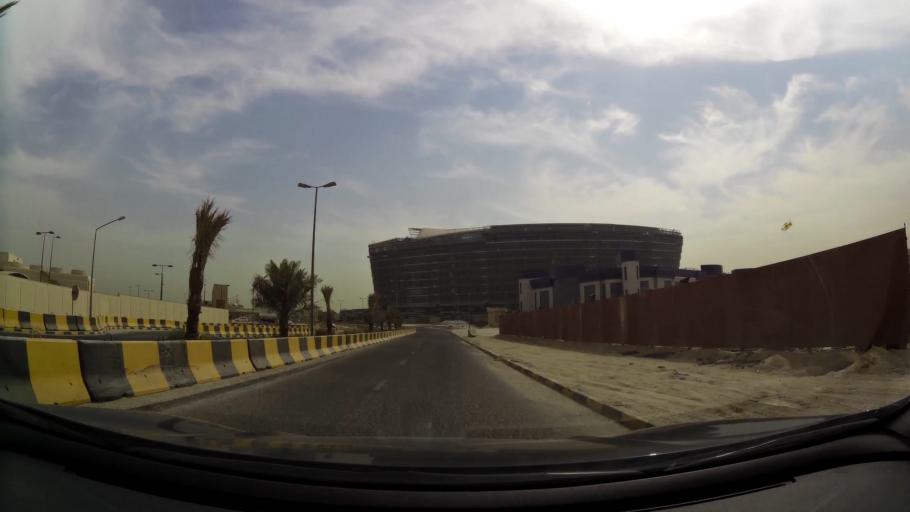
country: KW
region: Al Farwaniyah
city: Janub as Surrah
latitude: 29.2744
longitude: 48.0182
